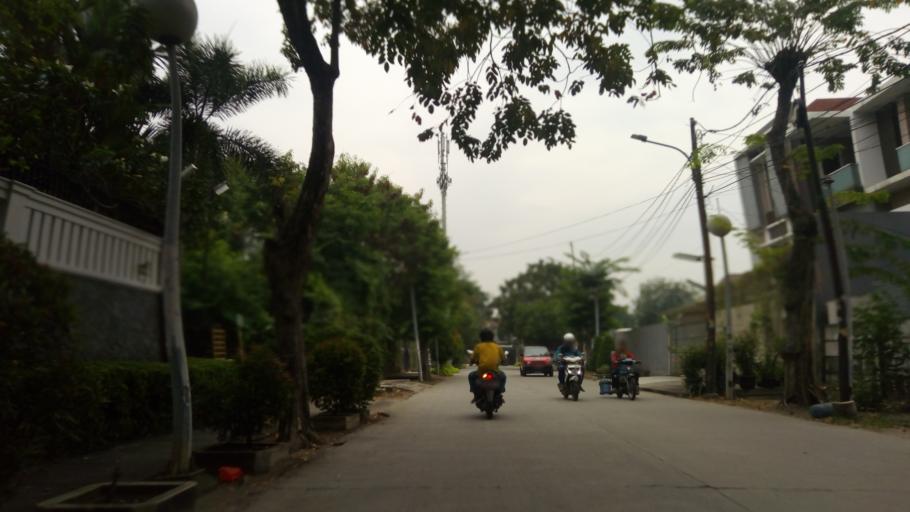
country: ID
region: Jakarta Raya
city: Jakarta
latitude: -6.1481
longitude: 106.8420
